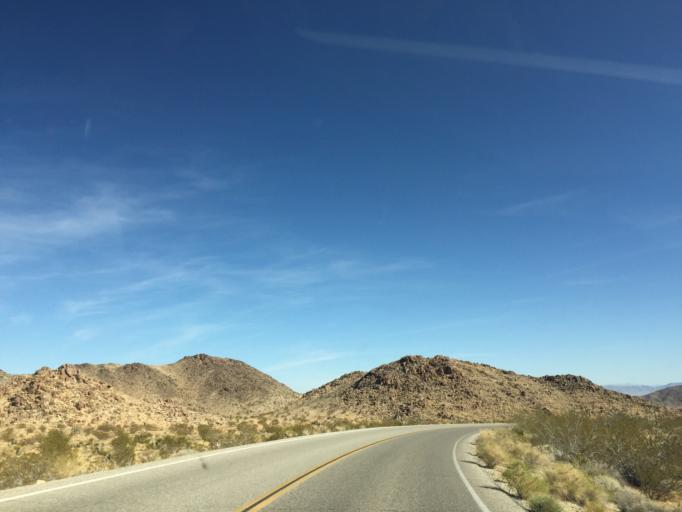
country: US
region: California
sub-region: San Bernardino County
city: Twentynine Palms
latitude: 34.0541
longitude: -116.0269
